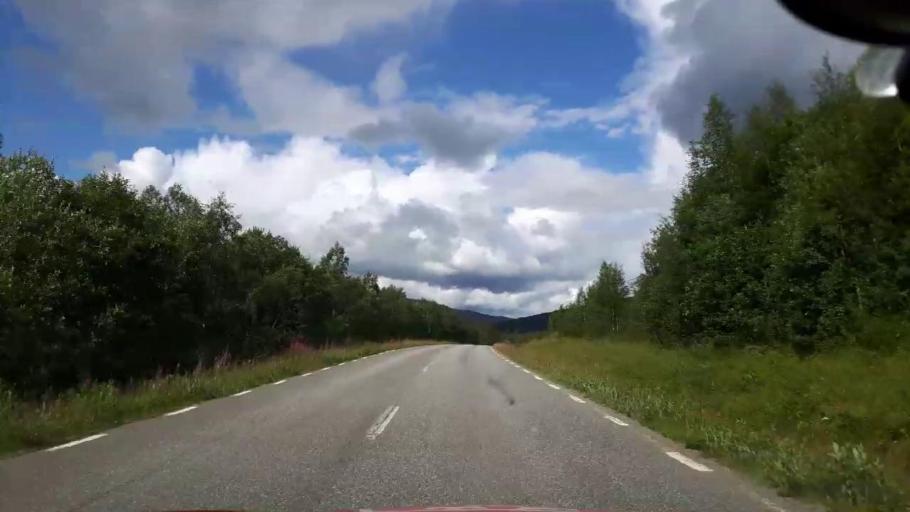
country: NO
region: Nordland
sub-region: Hattfjelldal
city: Hattfjelldal
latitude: 65.0541
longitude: 14.7327
